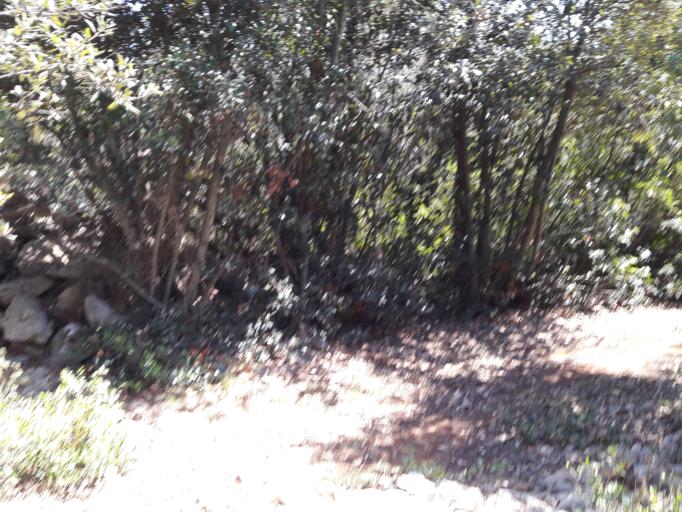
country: HR
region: Licko-Senjska
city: Novalja
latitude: 44.3643
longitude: 14.6984
